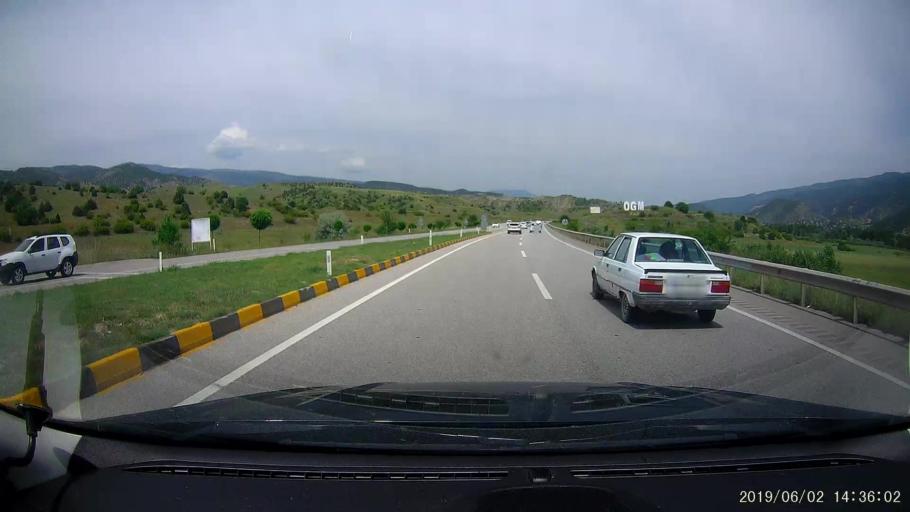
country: TR
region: Kastamonu
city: Tosya
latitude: 41.0438
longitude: 34.2271
